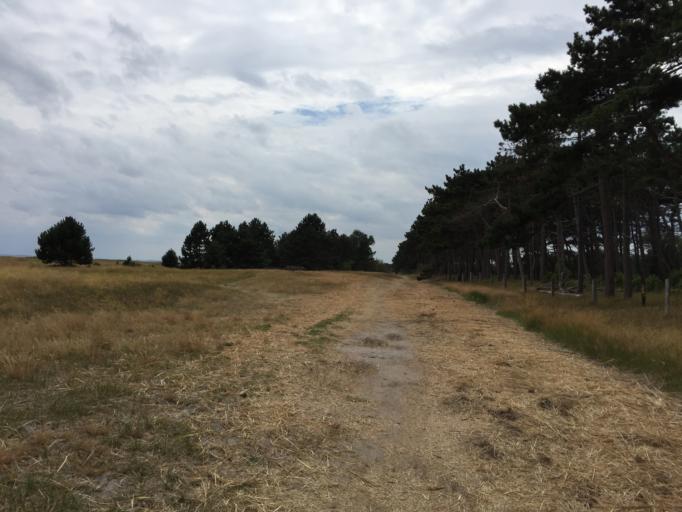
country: DE
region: Mecklenburg-Vorpommern
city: Hiddensee
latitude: 54.5123
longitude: 13.0777
